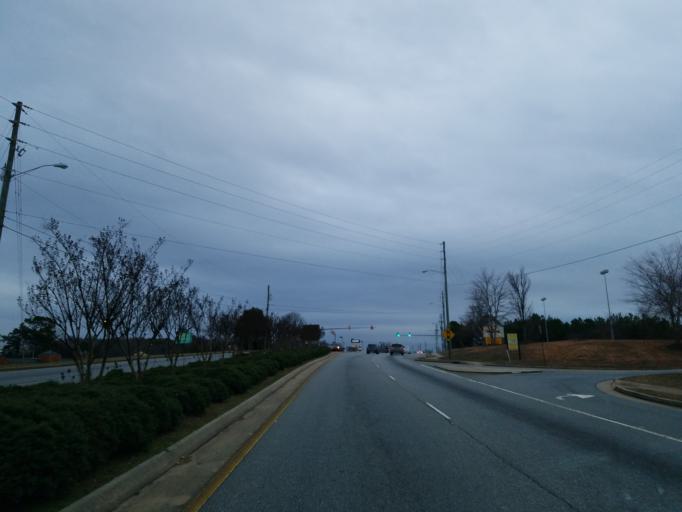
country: US
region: Georgia
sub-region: Cobb County
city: Acworth
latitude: 34.0778
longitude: -84.6765
